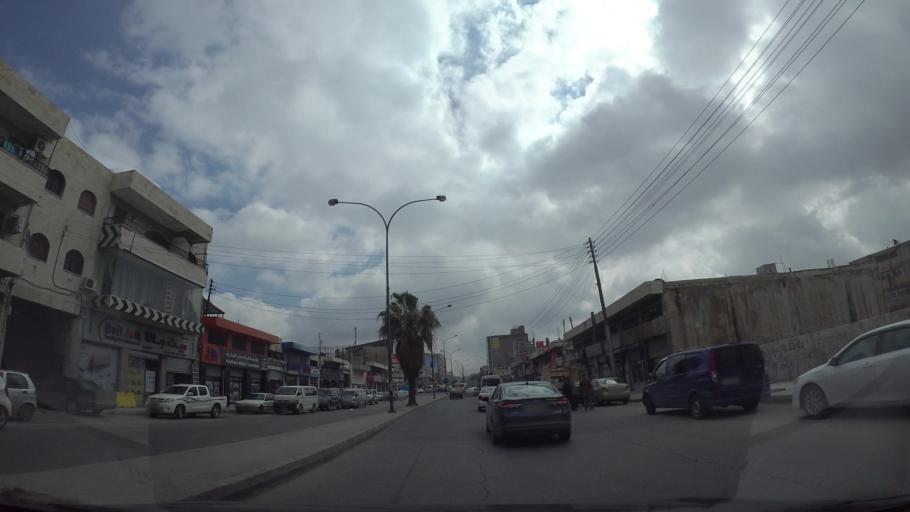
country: JO
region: Amman
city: Al Quwaysimah
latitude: 31.9225
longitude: 35.9381
